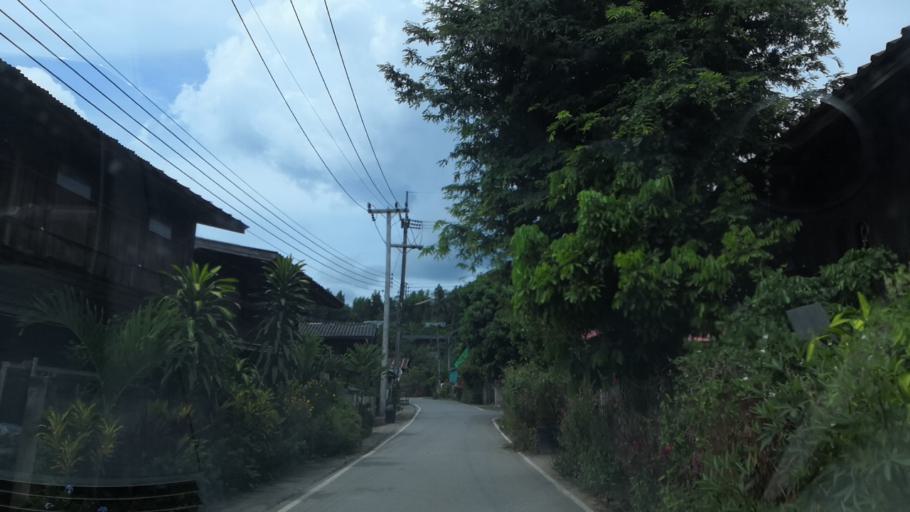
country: TH
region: Mae Hong Son
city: Khun Yuam
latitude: 18.7398
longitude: 97.9259
